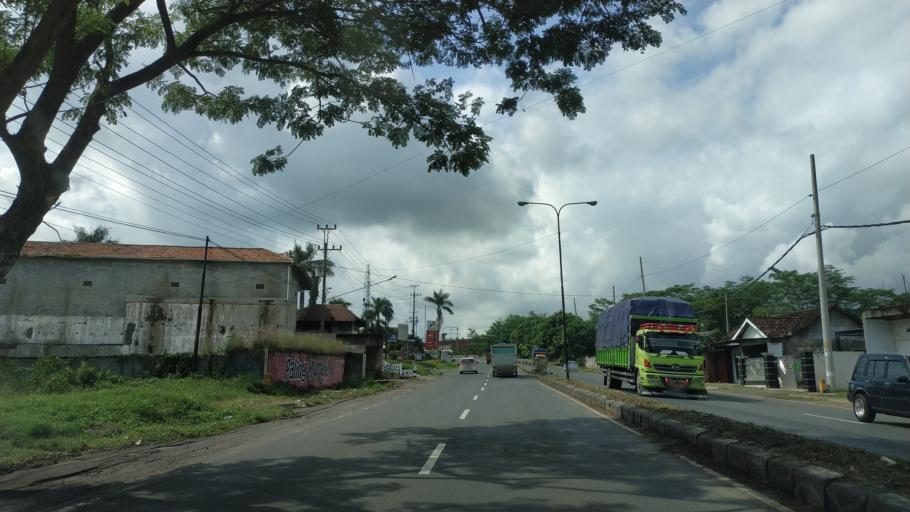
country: ID
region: Central Java
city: Pekalongan
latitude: -6.9452
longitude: 109.8201
